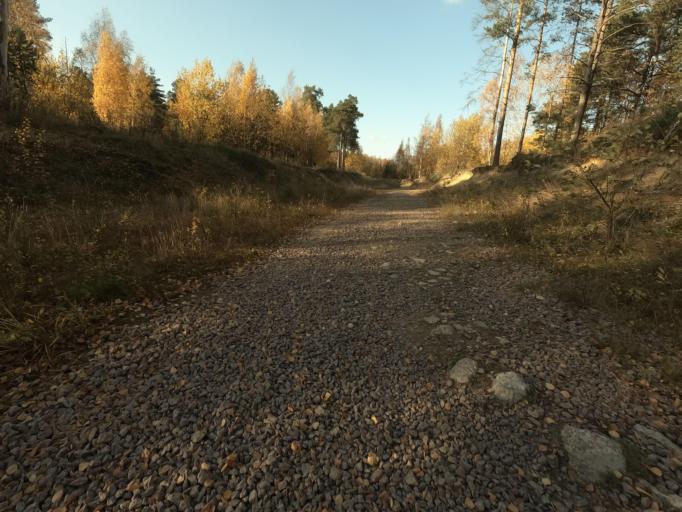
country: RU
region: Leningrad
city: Sertolovo
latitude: 60.1507
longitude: 30.2222
